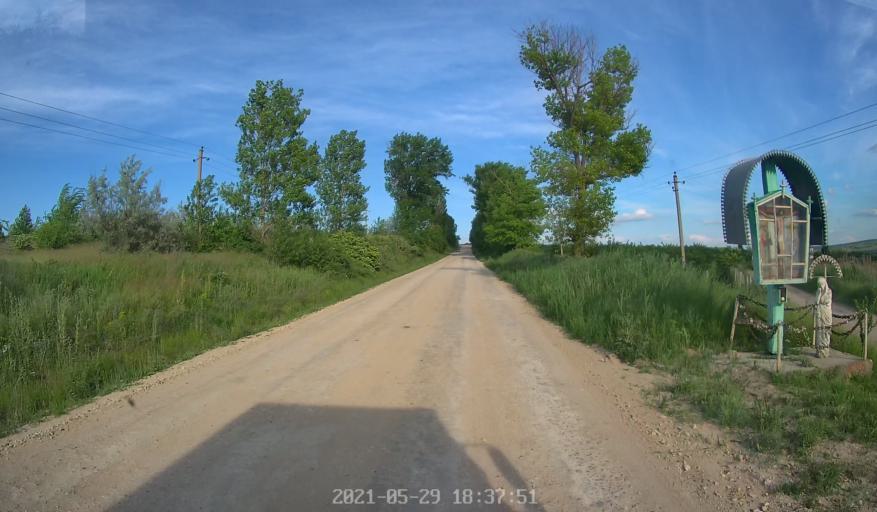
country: MD
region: Chisinau
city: Singera
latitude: 46.8033
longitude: 28.9337
